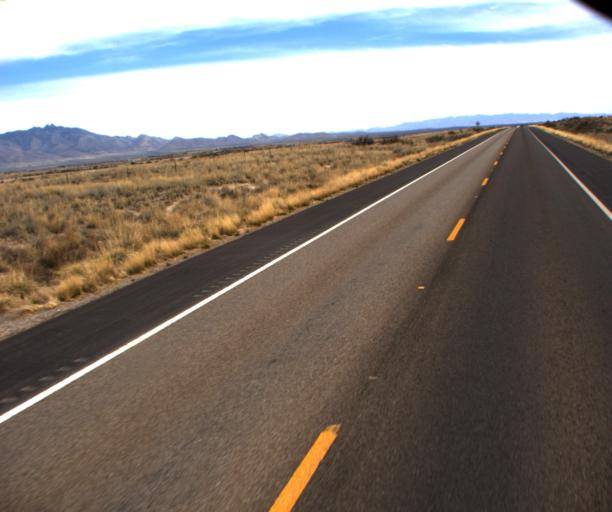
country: US
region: Arizona
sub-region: Cochise County
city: Willcox
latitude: 32.2315
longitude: -109.8024
